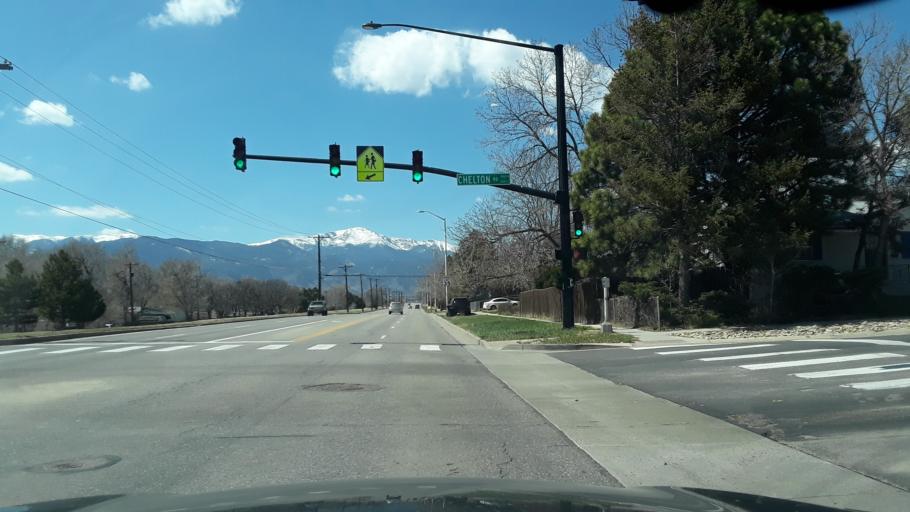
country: US
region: Colorado
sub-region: El Paso County
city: Colorado Springs
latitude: 38.8594
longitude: -104.7652
